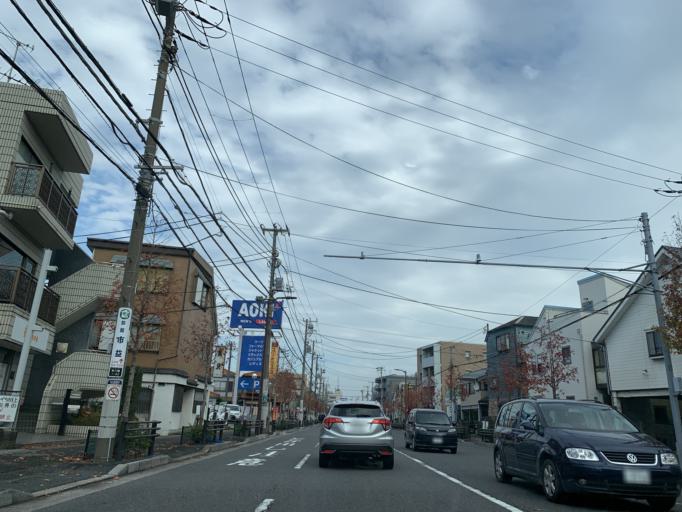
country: JP
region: Chiba
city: Funabashi
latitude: 35.7155
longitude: 139.9308
